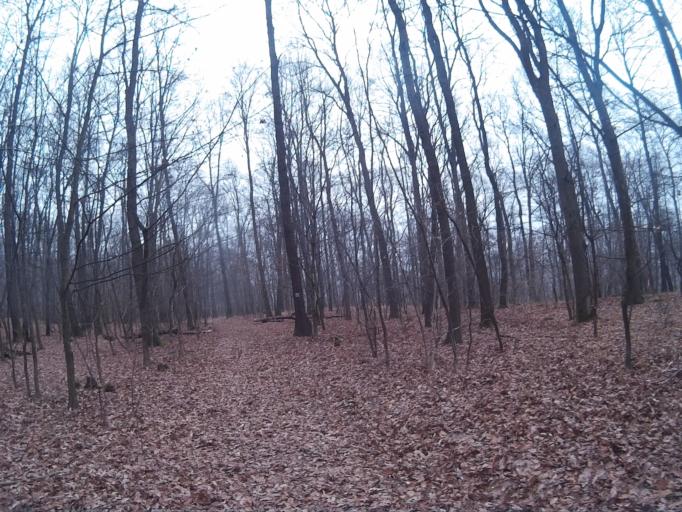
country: HU
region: Nograd
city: Rimoc
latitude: 47.9797
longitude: 19.5697
